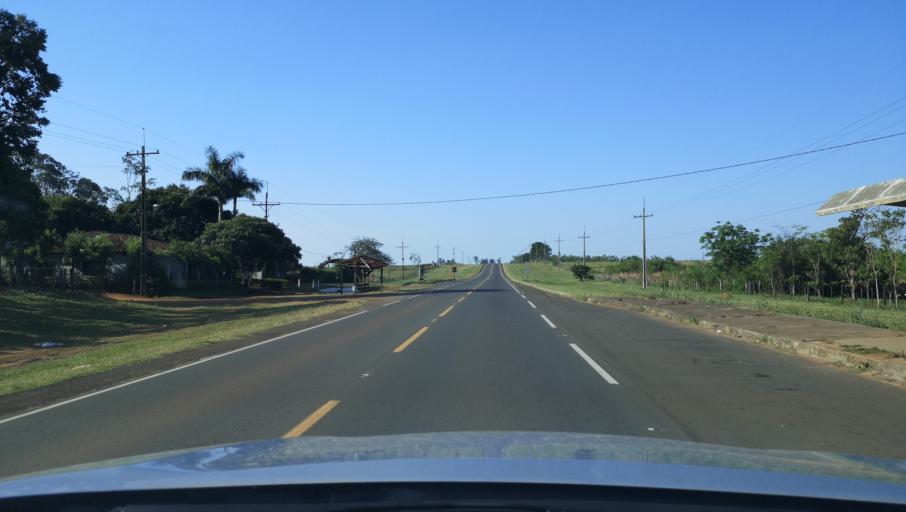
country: PY
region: Misiones
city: Santa Maria
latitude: -26.8157
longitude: -57.0239
